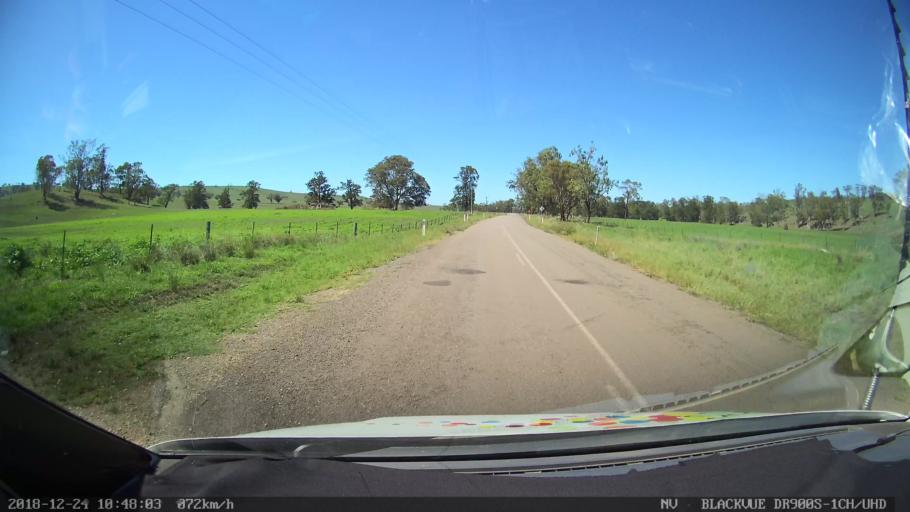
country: AU
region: New South Wales
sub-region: Upper Hunter Shire
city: Merriwa
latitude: -31.9316
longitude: 150.4298
